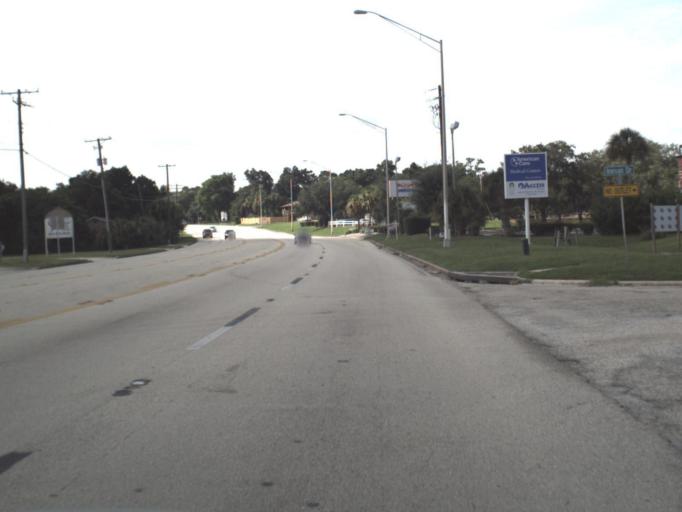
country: US
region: Florida
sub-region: Polk County
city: Winter Haven
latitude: 28.0528
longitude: -81.7345
